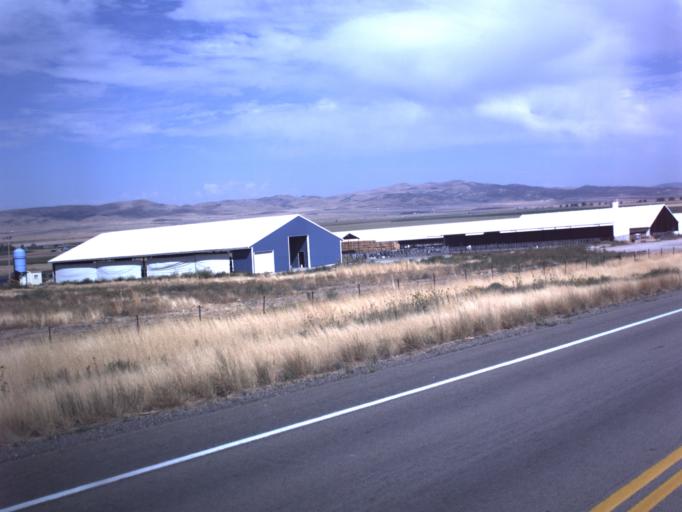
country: US
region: Utah
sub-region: Juab County
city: Nephi
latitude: 39.5171
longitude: -111.8680
